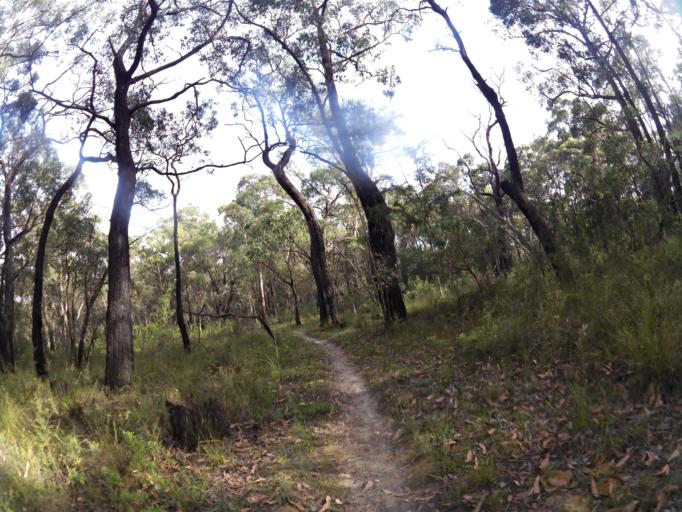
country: AU
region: Victoria
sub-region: Colac-Otway
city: Colac
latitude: -38.4890
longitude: 143.7160
